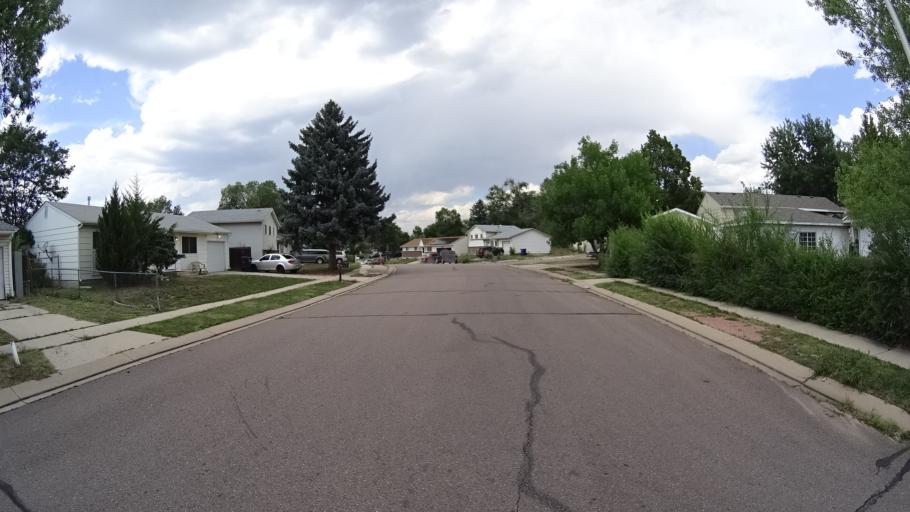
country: US
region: Colorado
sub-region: El Paso County
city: Cimarron Hills
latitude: 38.8297
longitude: -104.7469
